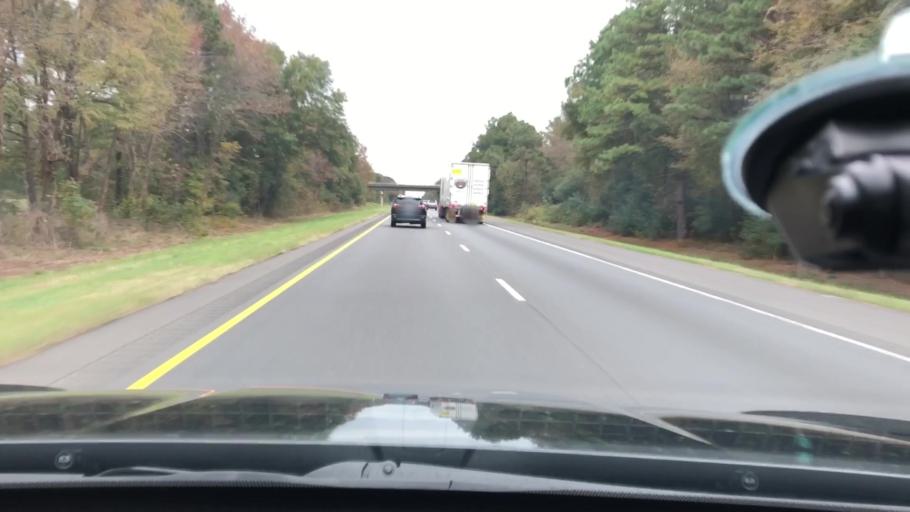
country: US
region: Arkansas
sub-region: Hempstead County
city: Hope
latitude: 33.7014
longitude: -93.5838
